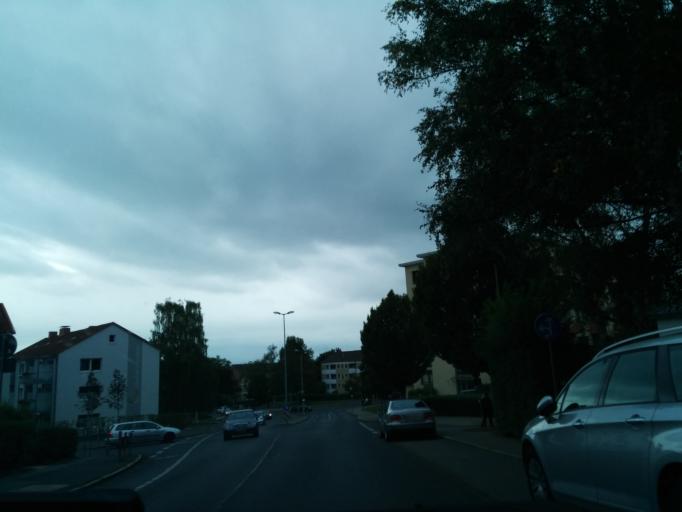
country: DE
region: Lower Saxony
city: Goettingen
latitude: 51.5268
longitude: 9.9557
